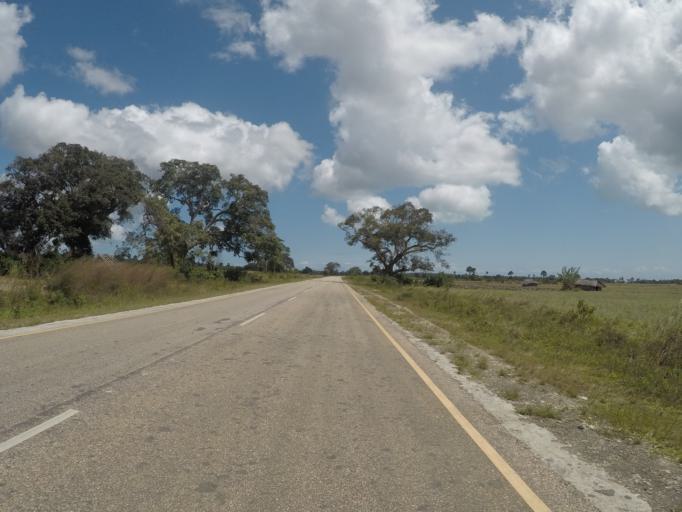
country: TZ
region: Zanzibar Central/South
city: Koani
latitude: -6.2127
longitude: 39.3654
